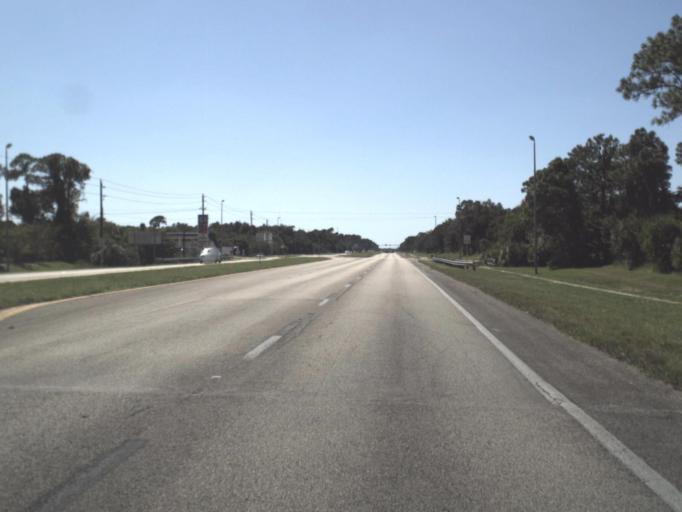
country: US
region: Florida
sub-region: Charlotte County
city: Port Charlotte
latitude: 27.0101
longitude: -82.1547
